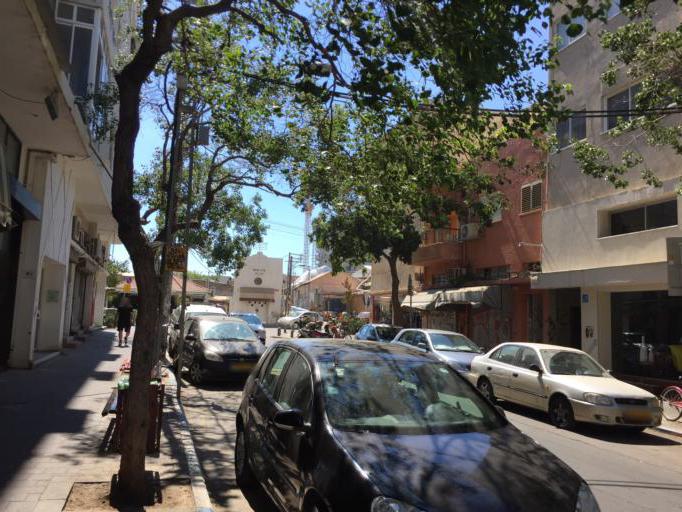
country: IL
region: Tel Aviv
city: Yafo
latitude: 32.0572
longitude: 34.7676
